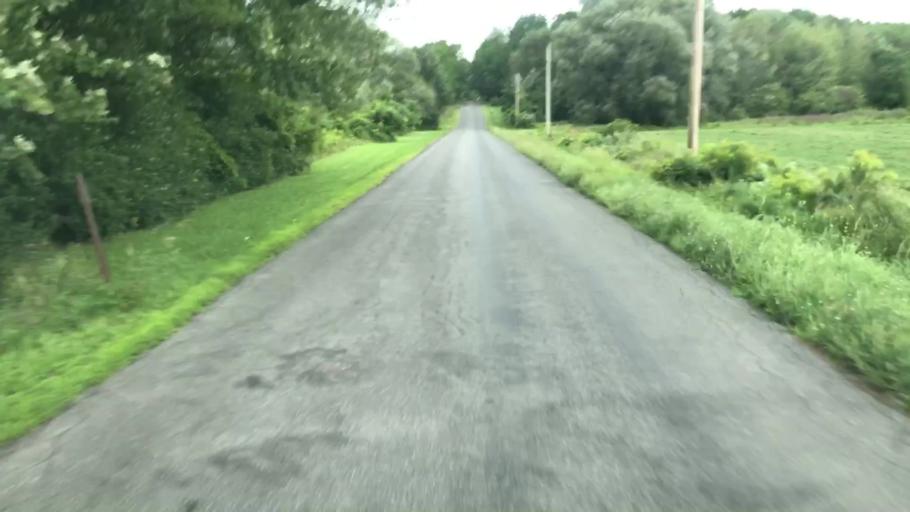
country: US
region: New York
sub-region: Onondaga County
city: Skaneateles
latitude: 42.9847
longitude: -76.4579
